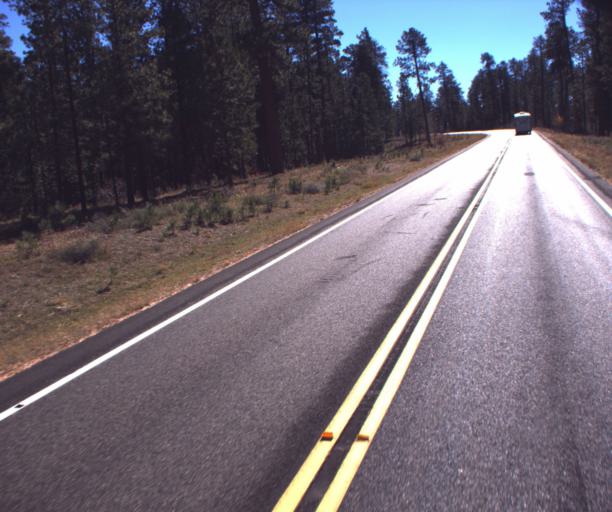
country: US
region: Arizona
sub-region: Coconino County
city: Fredonia
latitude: 36.6487
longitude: -112.1827
